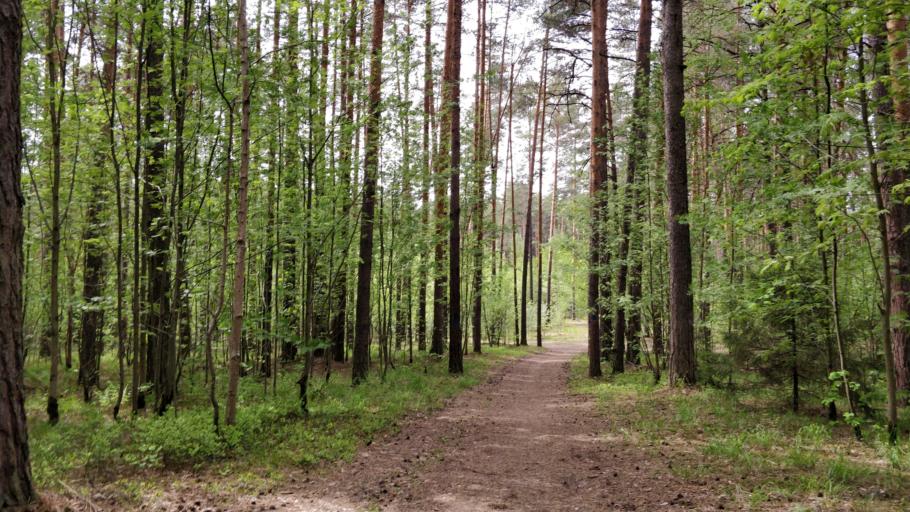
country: RU
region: Perm
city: Kondratovo
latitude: 57.9798
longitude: 56.1373
